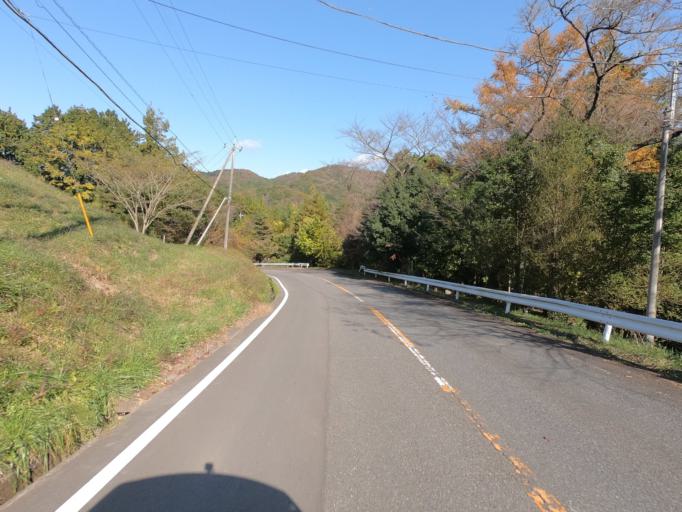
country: JP
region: Ibaraki
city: Makabe
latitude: 36.2343
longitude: 140.1283
